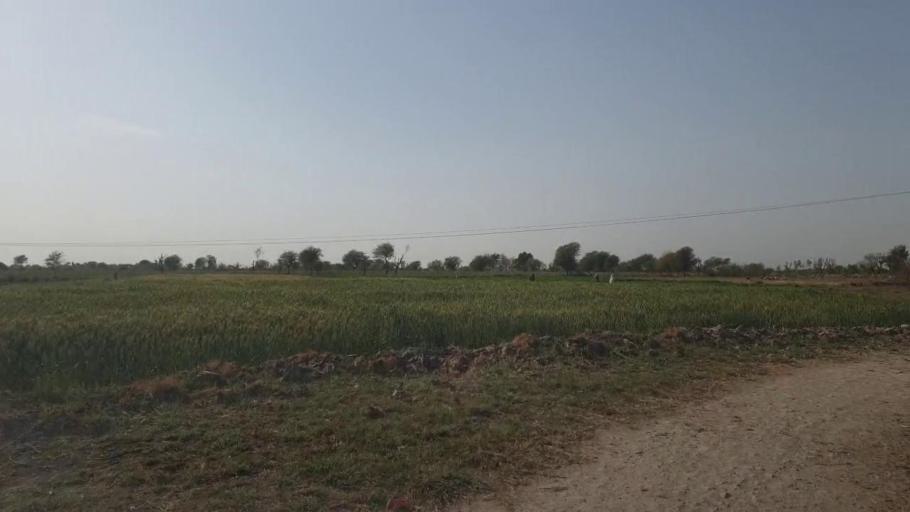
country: PK
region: Sindh
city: Dhoro Naro
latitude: 25.4696
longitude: 69.5397
